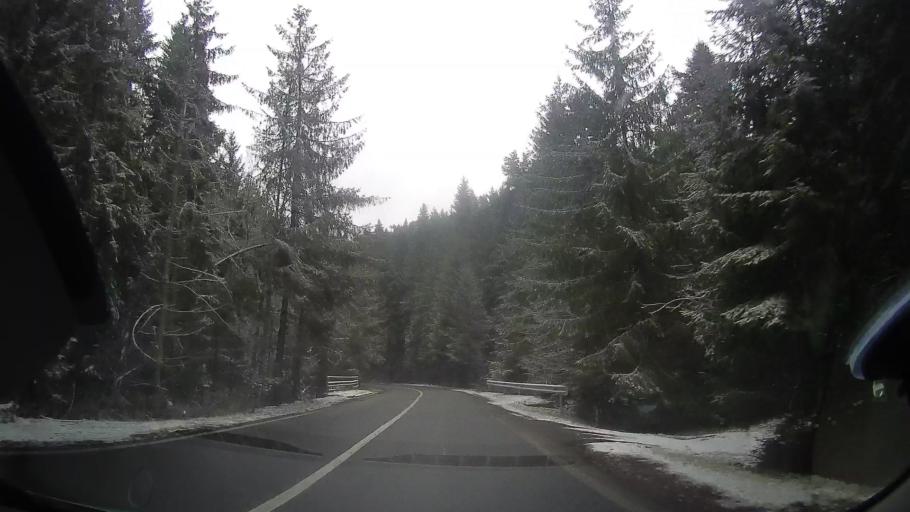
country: RO
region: Cluj
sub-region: Comuna Calatele
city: Calatele
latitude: 46.7317
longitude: 23.0377
